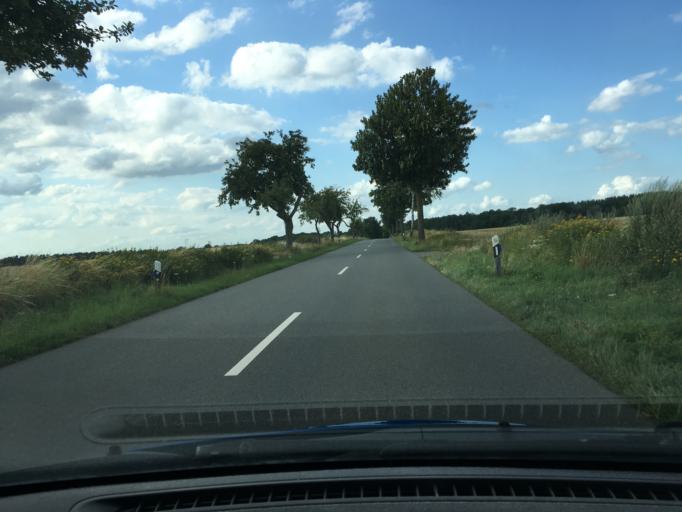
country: DE
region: Lower Saxony
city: Altenmedingen
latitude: 53.1620
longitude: 10.6190
